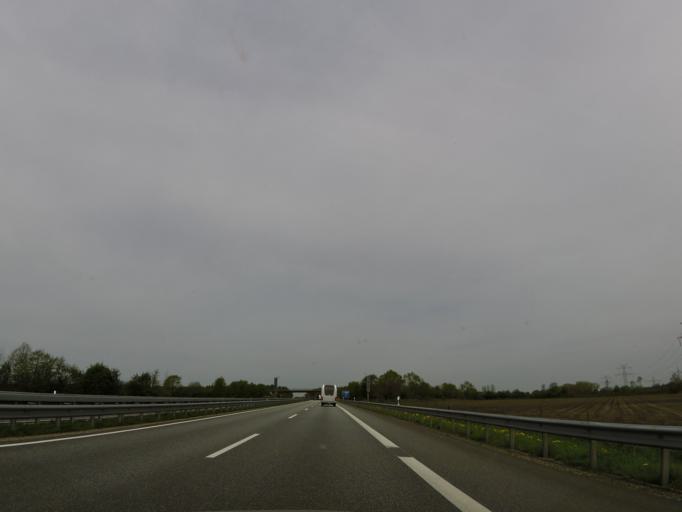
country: DE
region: Schleswig-Holstein
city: Kaisborstel
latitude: 54.0023
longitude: 9.4815
